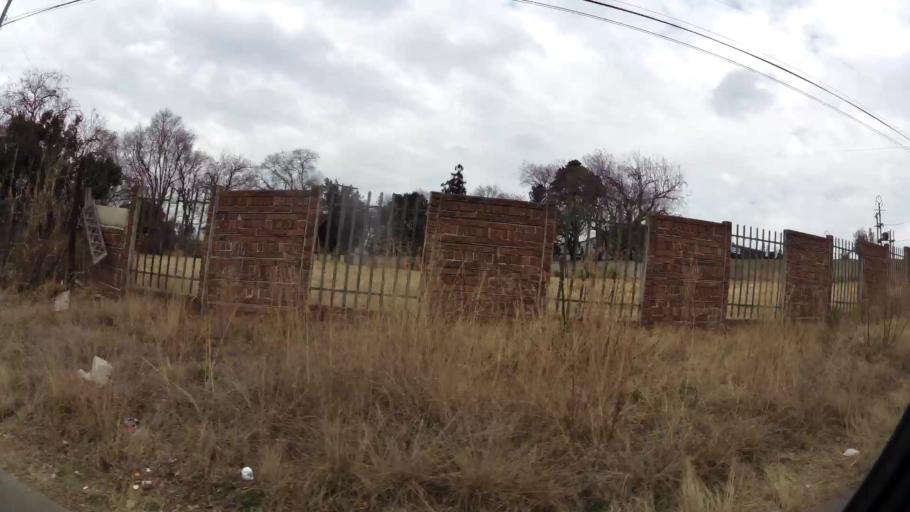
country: ZA
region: Gauteng
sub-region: West Rand District Municipality
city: Muldersdriseloop
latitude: -26.0389
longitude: 27.8457
